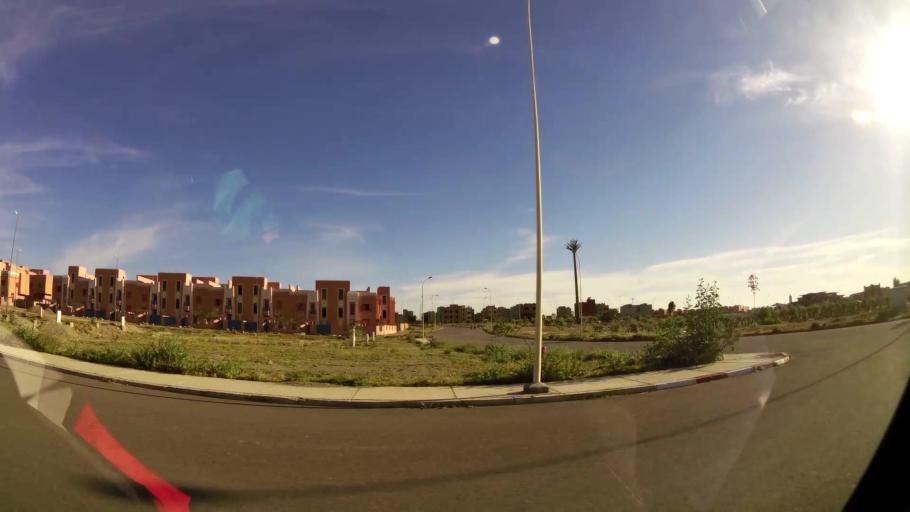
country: MA
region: Marrakech-Tensift-Al Haouz
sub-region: Marrakech
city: Marrakesh
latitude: 31.7555
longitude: -8.1050
